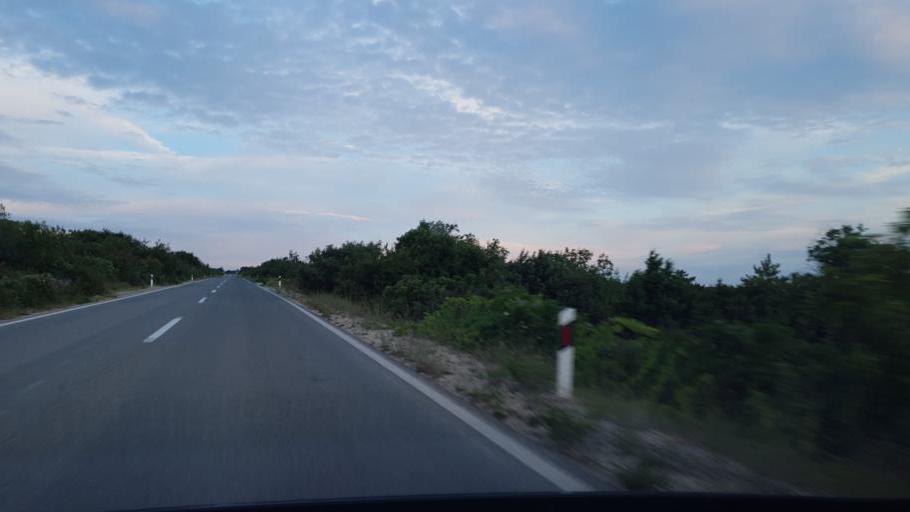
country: HR
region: Primorsko-Goranska
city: Punat
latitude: 45.0414
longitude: 14.6411
